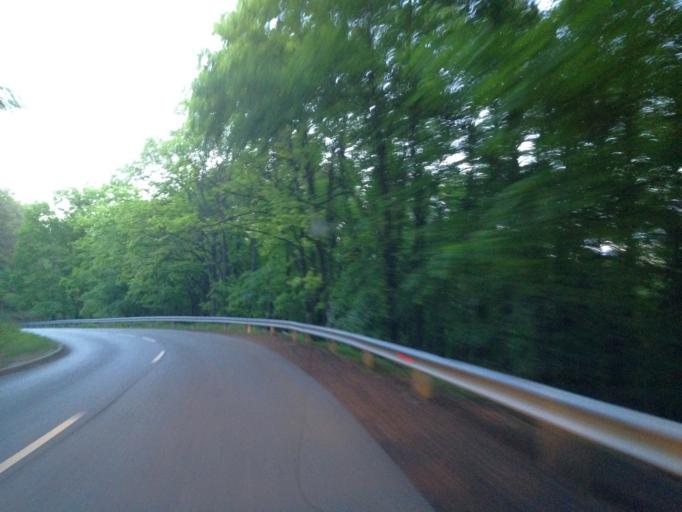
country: HU
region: Nograd
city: Batonyterenye
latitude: 47.8992
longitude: 19.8833
